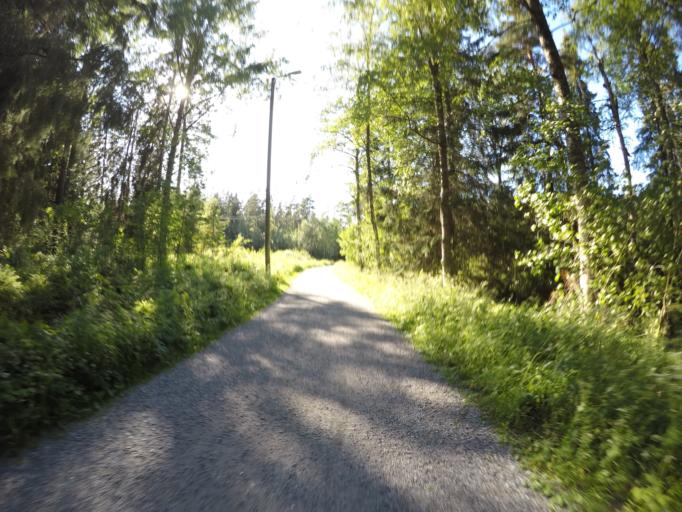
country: FI
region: Haeme
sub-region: Haemeenlinna
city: Haemeenlinna
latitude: 61.0189
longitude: 24.4897
